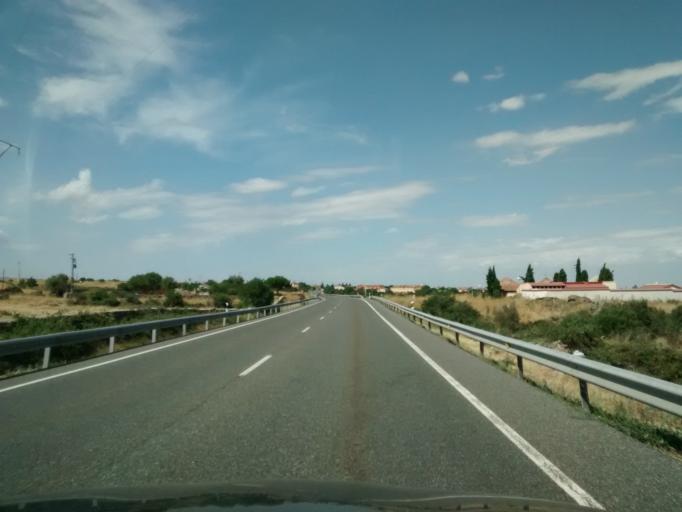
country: ES
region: Castille and Leon
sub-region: Provincia de Segovia
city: Torrecaballeros
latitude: 41.0023
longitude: -4.0116
